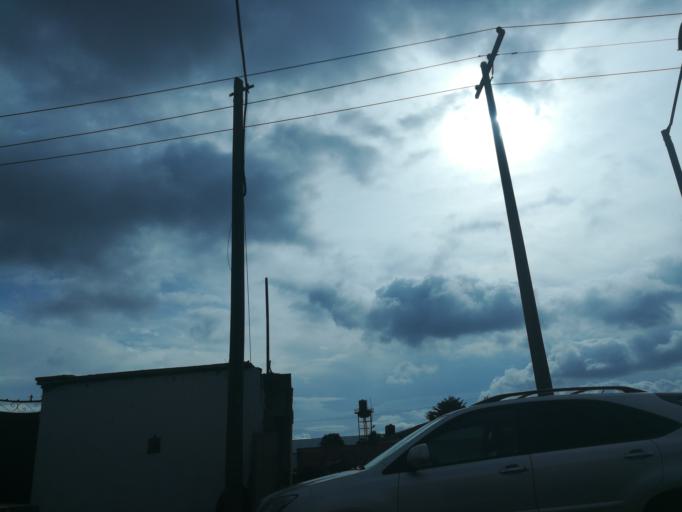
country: NG
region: Lagos
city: Ikeja
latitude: 6.6161
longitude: 3.3565
